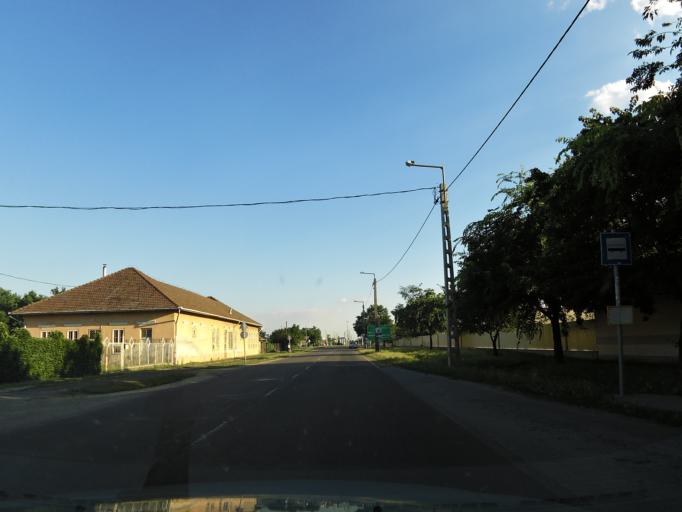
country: HU
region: Jasz-Nagykun-Szolnok
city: Rakocziujfalu
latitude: 47.0201
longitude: 20.2913
